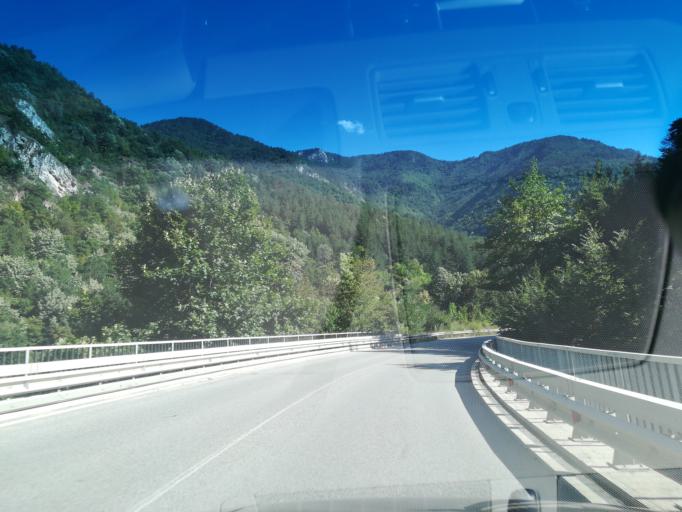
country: BG
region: Plovdiv
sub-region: Obshtina Asenovgrad
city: Asenovgrad
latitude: 41.9354
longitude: 24.8502
